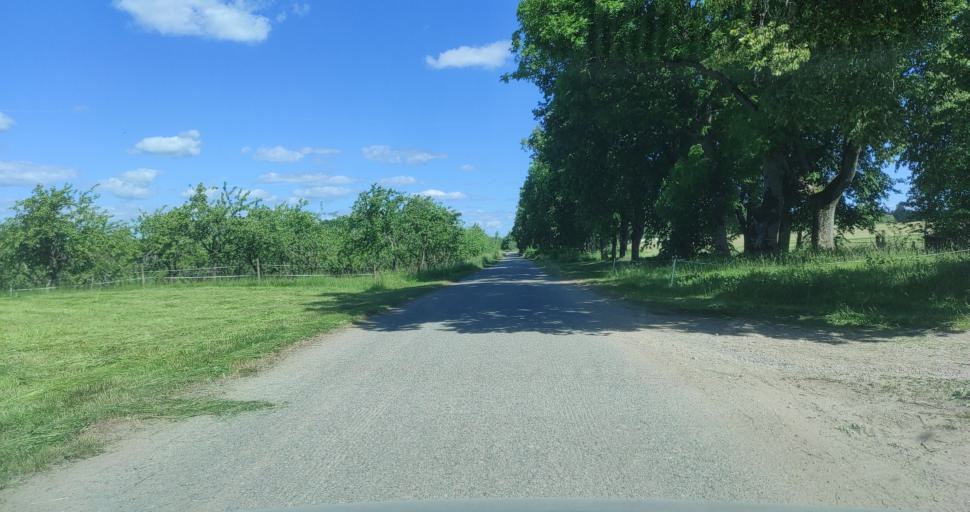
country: LV
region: Kuldigas Rajons
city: Kuldiga
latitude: 56.9378
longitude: 21.8251
